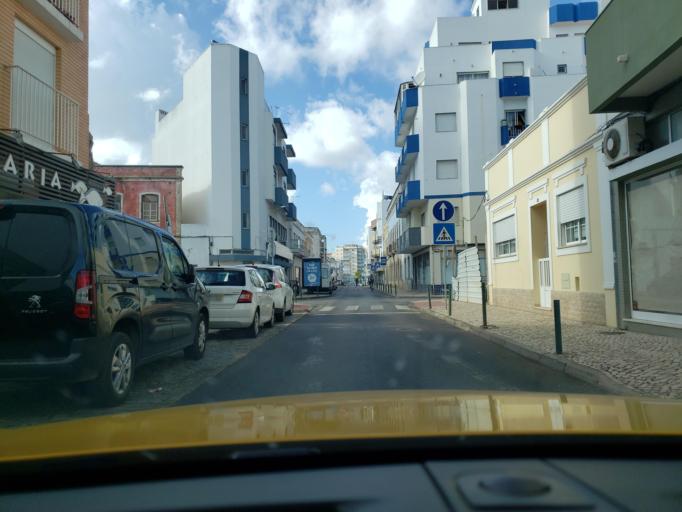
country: PT
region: Faro
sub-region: Portimao
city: Portimao
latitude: 37.1422
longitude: -8.5366
